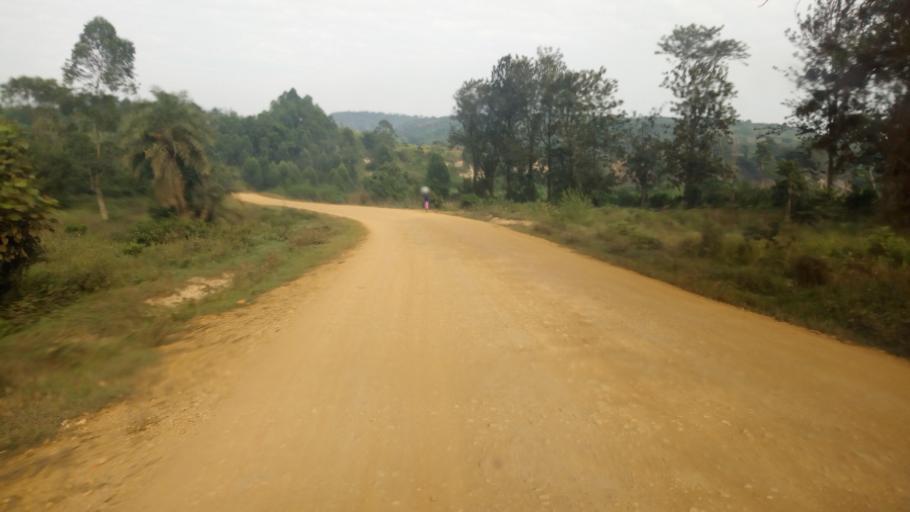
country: UG
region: Western Region
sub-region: Kanungu District
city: Ntungamo
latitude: -0.8388
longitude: 29.6422
